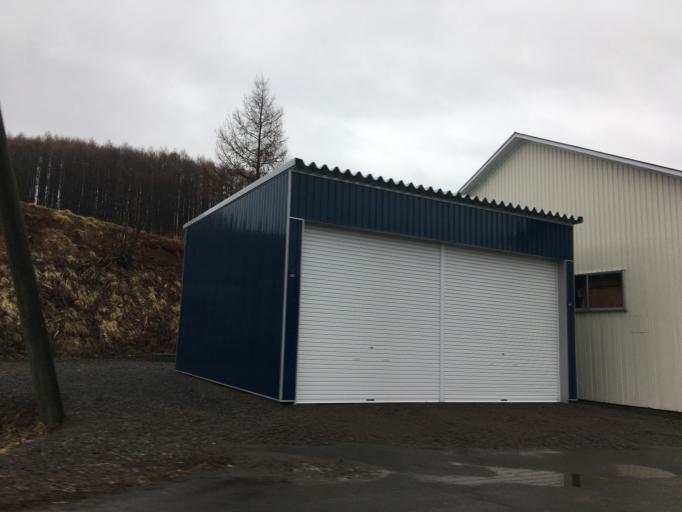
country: JP
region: Hokkaido
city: Nayoro
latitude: 44.0717
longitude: 142.4131
